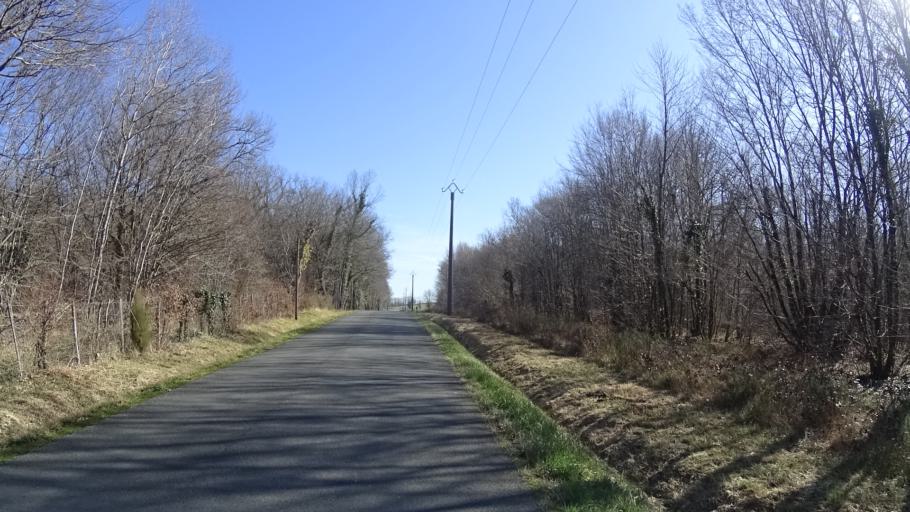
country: FR
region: Aquitaine
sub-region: Departement de la Dordogne
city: Saint-Aulaye
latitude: 45.1281
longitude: 0.2449
